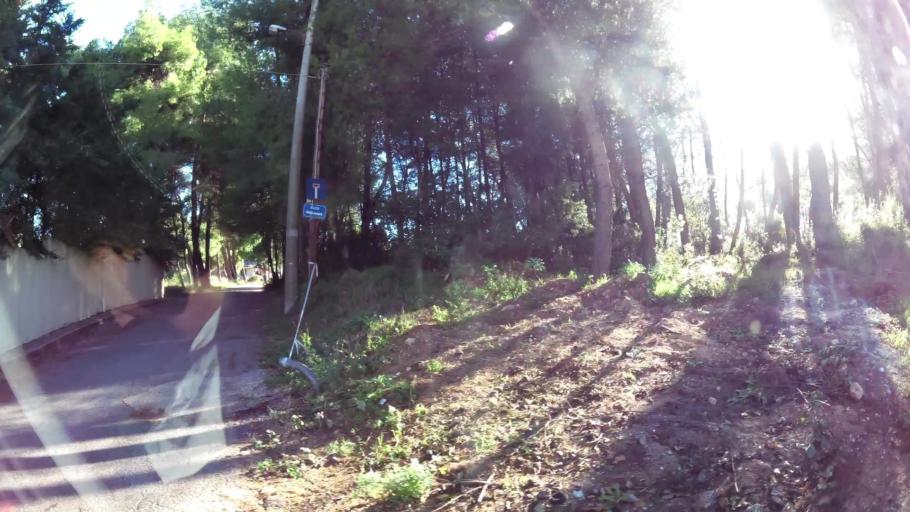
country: GR
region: Attica
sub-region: Nomarchia Anatolikis Attikis
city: Drosia
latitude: 38.1275
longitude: 23.8680
